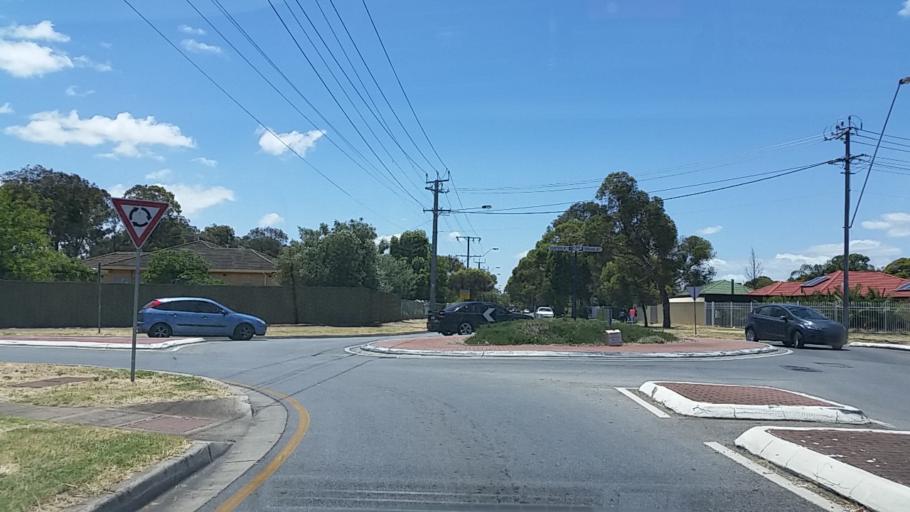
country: AU
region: South Australia
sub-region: Salisbury
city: Salisbury
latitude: -34.7661
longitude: 138.6258
